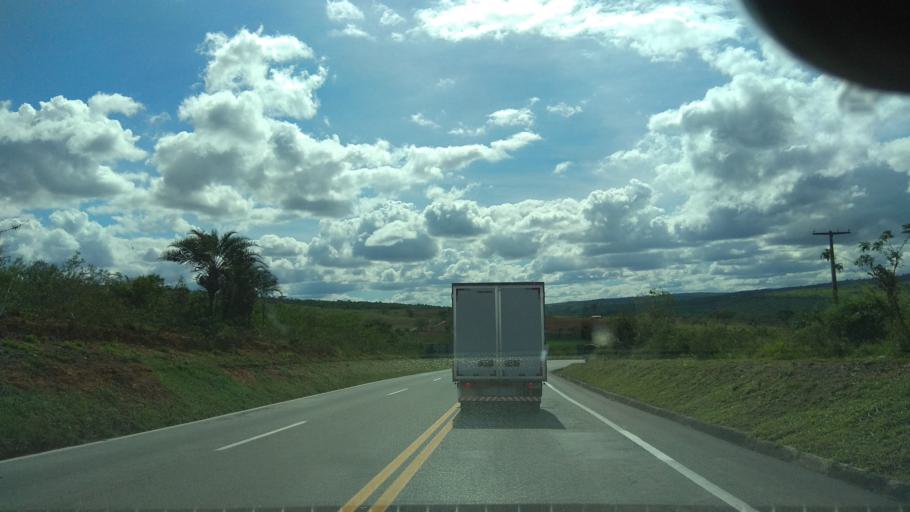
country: BR
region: Bahia
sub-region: Santa Ines
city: Santa Ines
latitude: -13.1657
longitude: -39.9985
